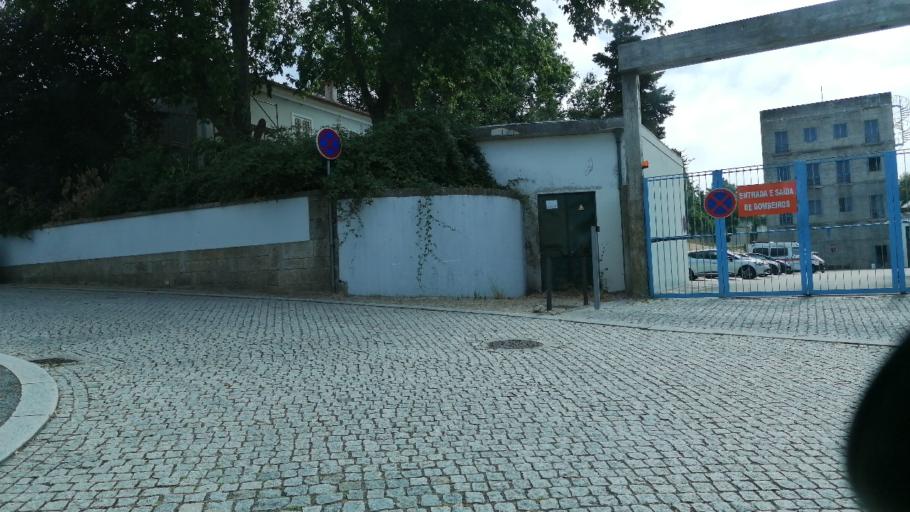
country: PT
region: Porto
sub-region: Matosinhos
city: Senhora da Hora
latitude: 41.1716
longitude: -8.6422
